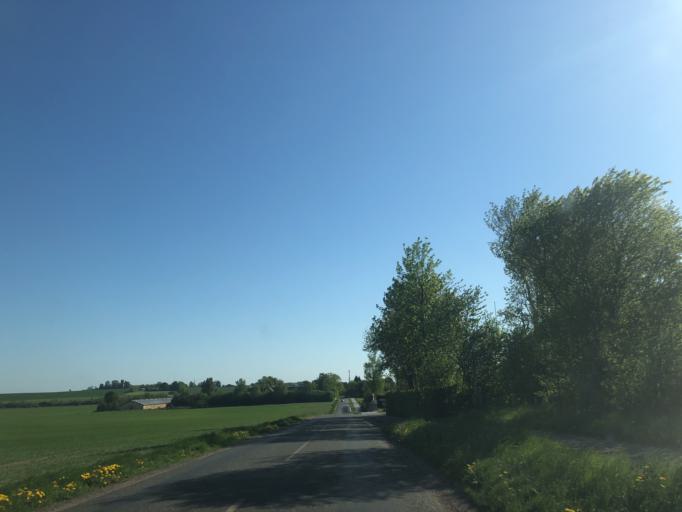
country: DK
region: Zealand
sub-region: Ringsted Kommune
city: Ringsted
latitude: 55.4449
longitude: 11.7288
